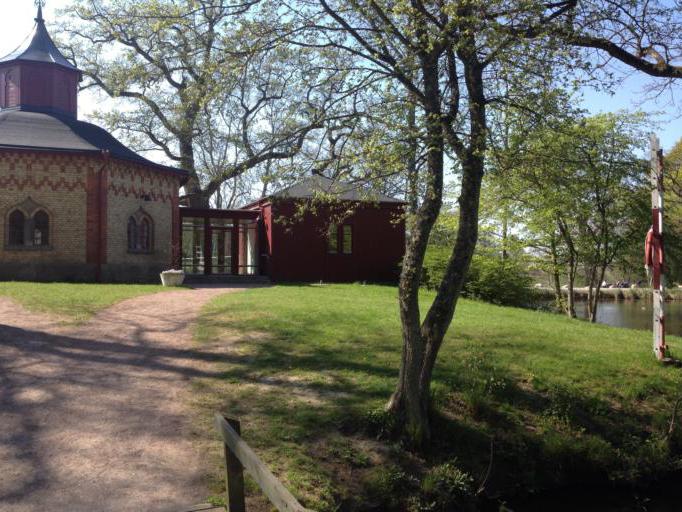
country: SE
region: Skane
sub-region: Svedala Kommun
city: Klagerup
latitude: 55.5670
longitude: 13.2124
